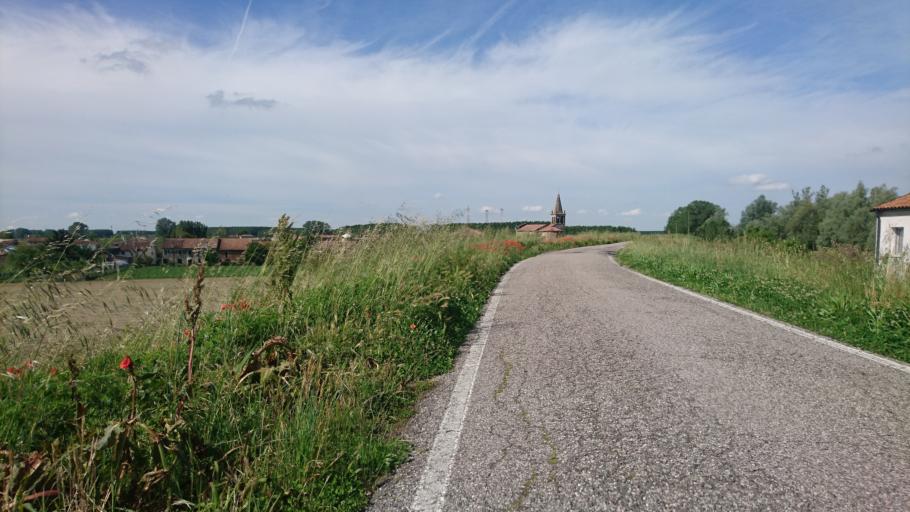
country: IT
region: Veneto
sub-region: Provincia di Rovigo
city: Melara
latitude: 45.0482
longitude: 11.1807
